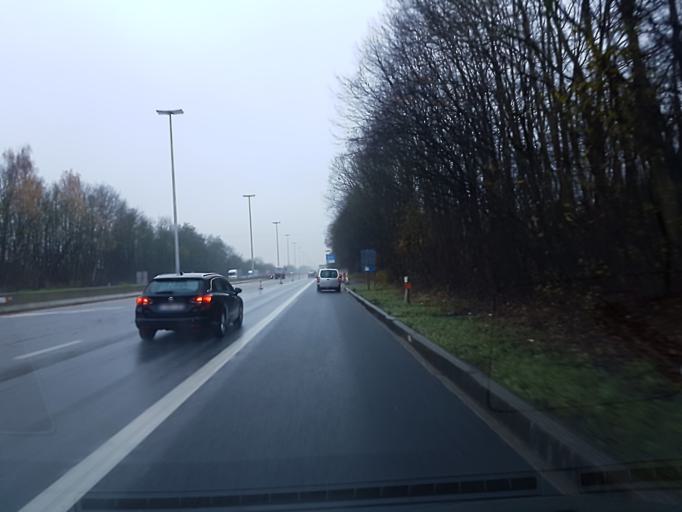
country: BE
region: Wallonia
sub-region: Province de Liege
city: Heron
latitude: 50.5303
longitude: 5.0686
